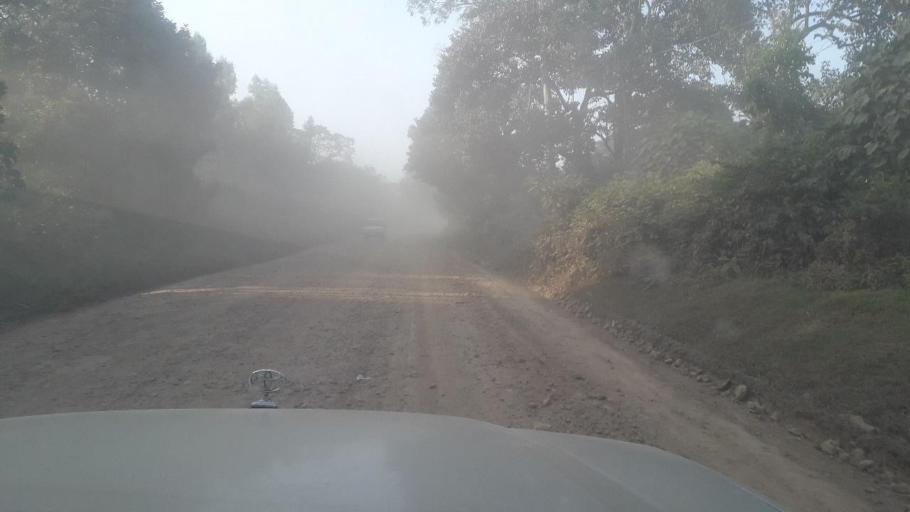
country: ET
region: Oromiya
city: Jima
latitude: 7.6278
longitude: 36.8296
